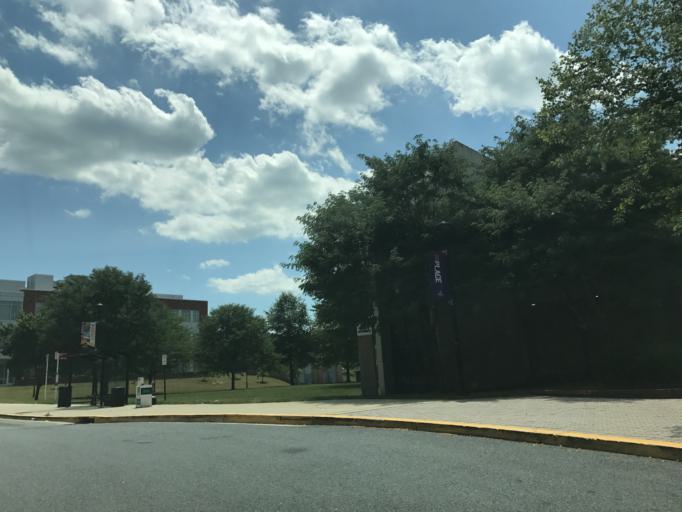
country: US
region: Maryland
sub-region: Prince George's County
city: Glenn Dale
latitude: 39.0180
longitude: -76.7612
